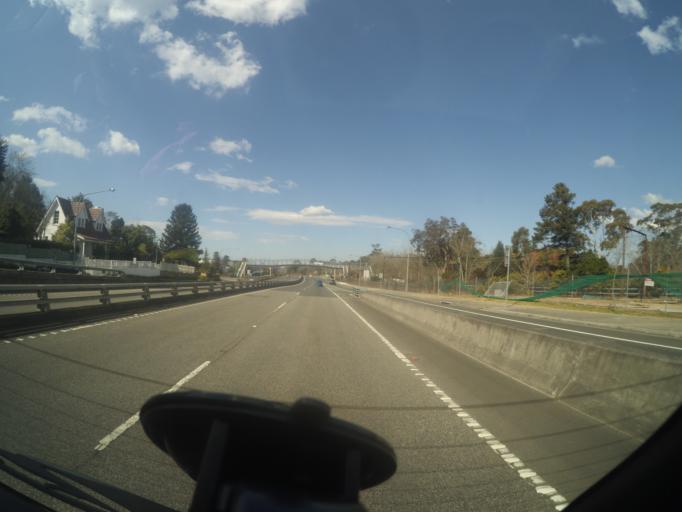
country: AU
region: New South Wales
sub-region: Blue Mountains Municipality
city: Leura
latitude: -33.7115
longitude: 150.3343
